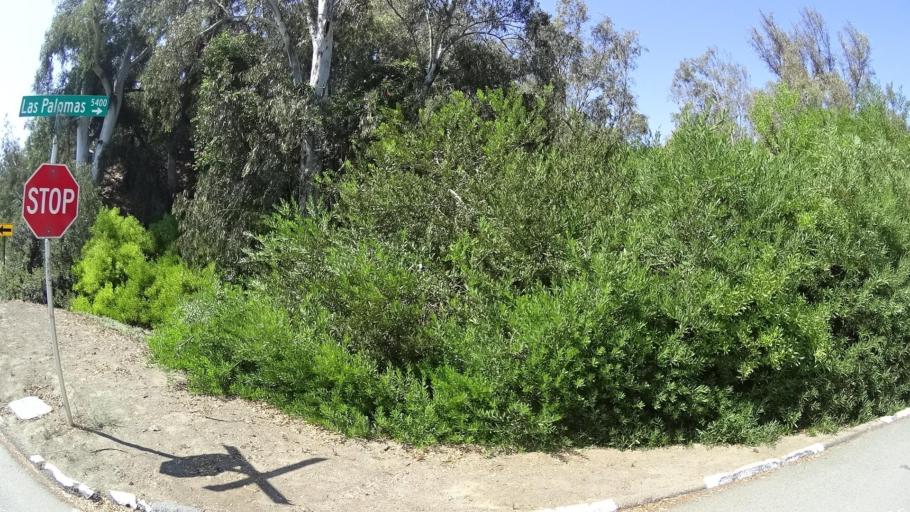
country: US
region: California
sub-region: San Diego County
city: Fairbanks Ranch
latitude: 32.9899
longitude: -117.2170
